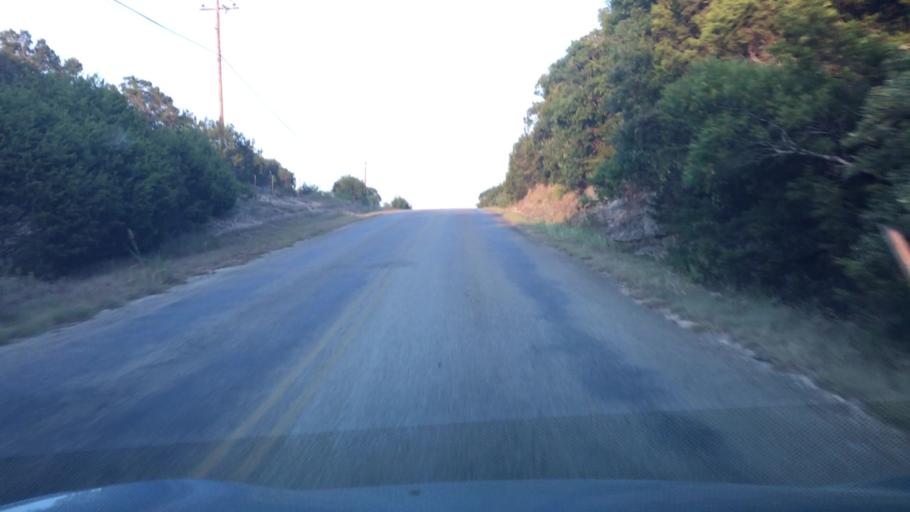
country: US
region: Texas
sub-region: Hays County
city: Dripping Springs
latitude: 30.1532
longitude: -98.0218
